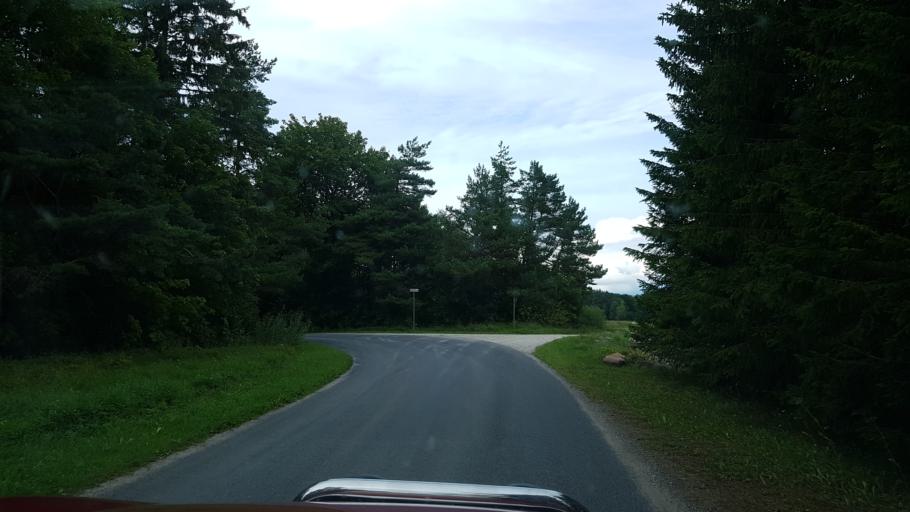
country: EE
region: Laeaene
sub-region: Ridala Parish
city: Uuemoisa
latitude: 59.0067
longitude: 23.7244
